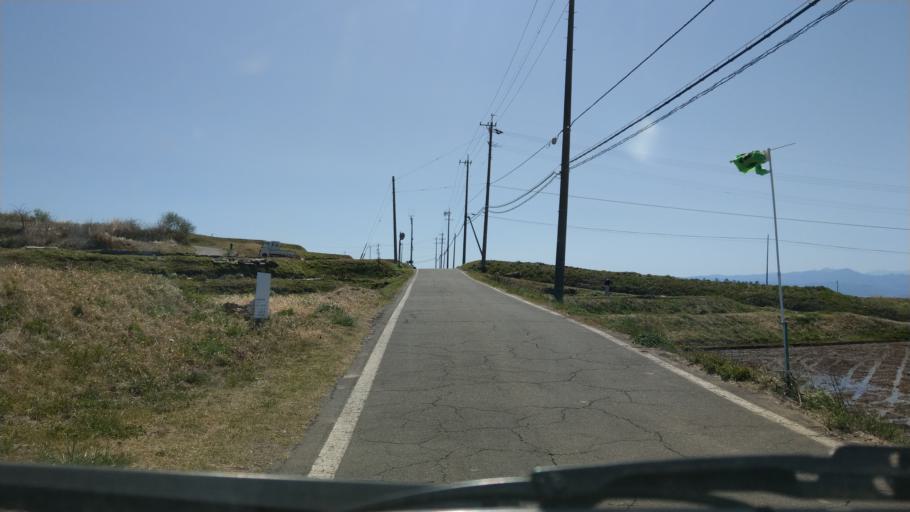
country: JP
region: Nagano
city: Komoro
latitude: 36.3552
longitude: 138.3952
